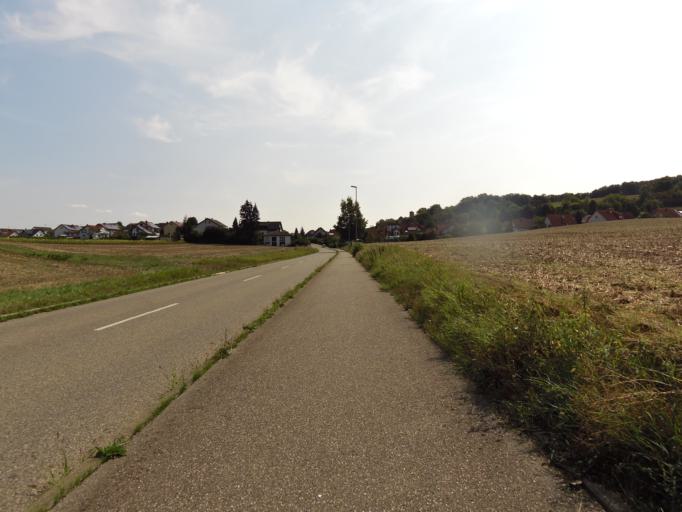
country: DE
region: Baden-Wuerttemberg
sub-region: Karlsruhe Region
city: Neidenstein
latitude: 49.3184
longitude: 8.8768
